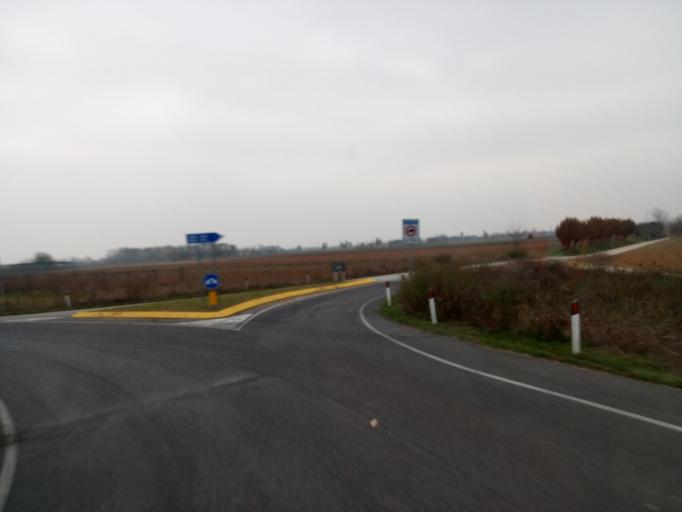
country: IT
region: Friuli Venezia Giulia
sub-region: Provincia di Udine
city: Buttrio
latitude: 46.0278
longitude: 13.3284
